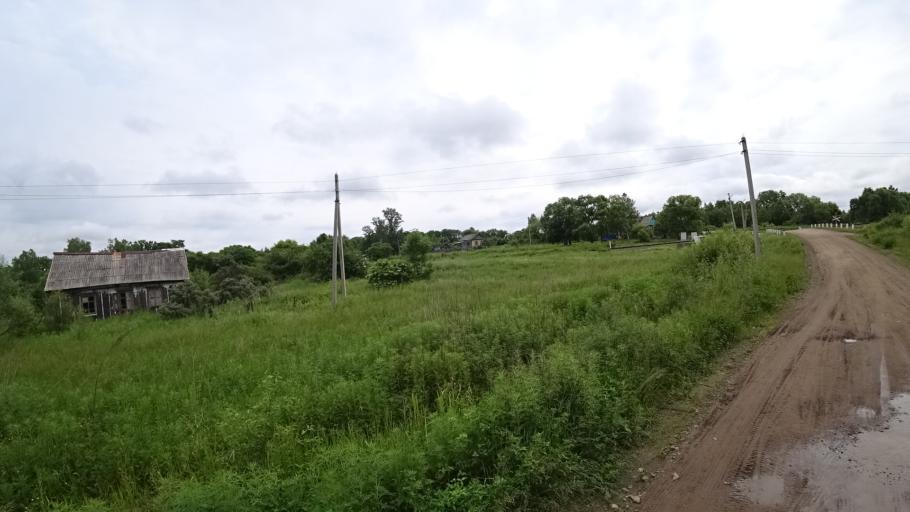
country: RU
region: Primorskiy
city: Novosysoyevka
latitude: 44.2535
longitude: 133.3746
